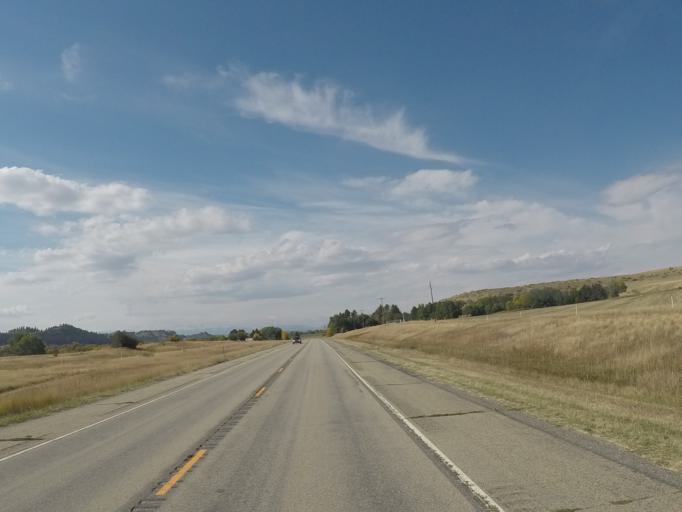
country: US
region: Montana
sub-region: Yellowstone County
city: Laurel
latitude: 45.4986
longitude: -108.9364
